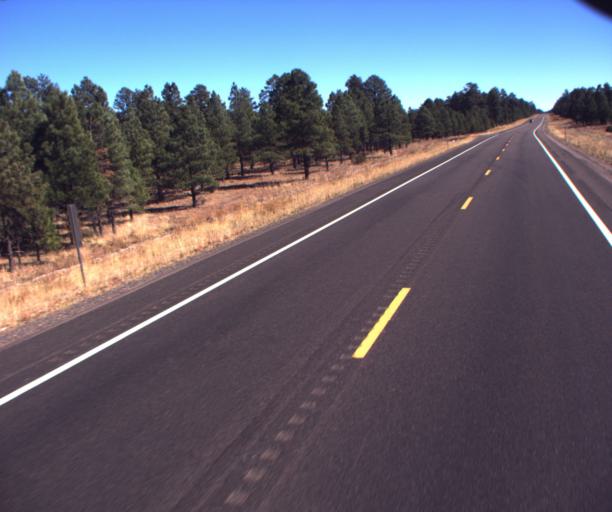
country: US
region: Arizona
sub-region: Apache County
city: Saint Michaels
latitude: 35.6977
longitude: -109.2806
